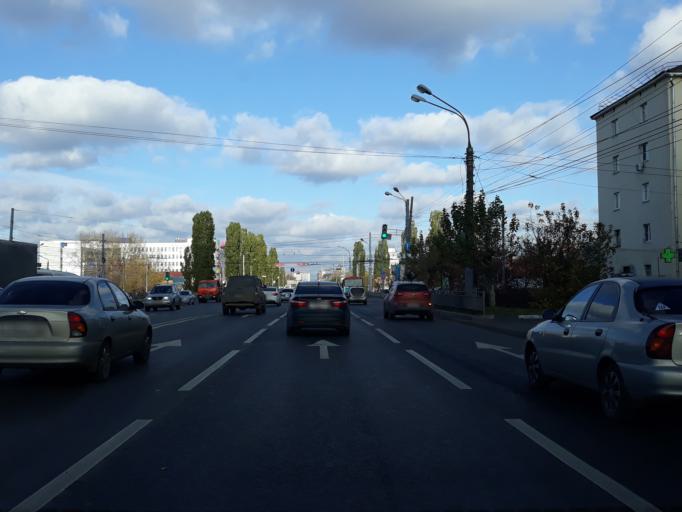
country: RU
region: Nizjnij Novgorod
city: Nizhniy Novgorod
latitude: 56.2834
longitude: 43.9268
